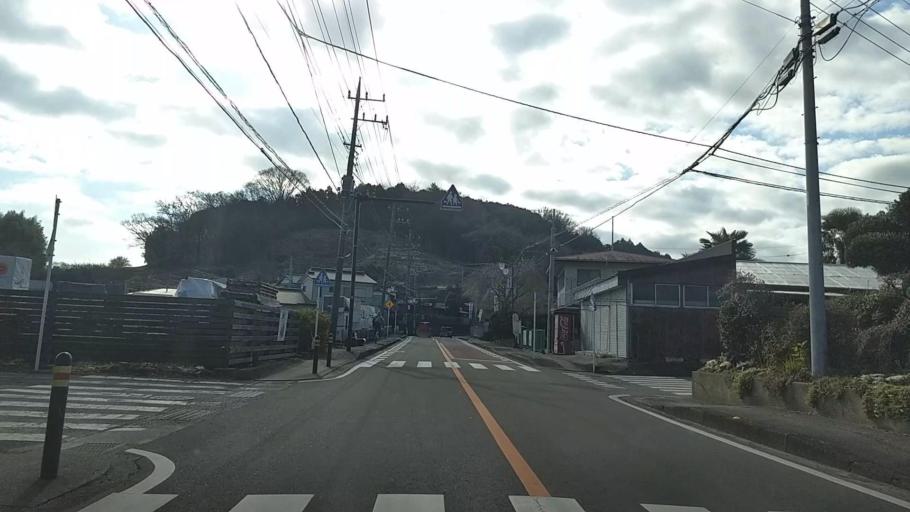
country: JP
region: Kanagawa
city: Isehara
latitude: 35.4395
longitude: 139.3017
